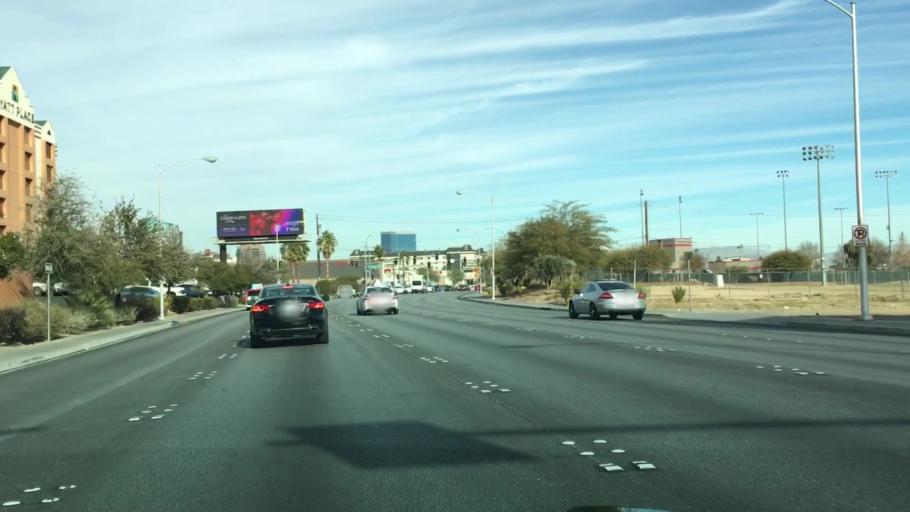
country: US
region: Nevada
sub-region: Clark County
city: Paradise
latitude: 36.1064
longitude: -115.1501
